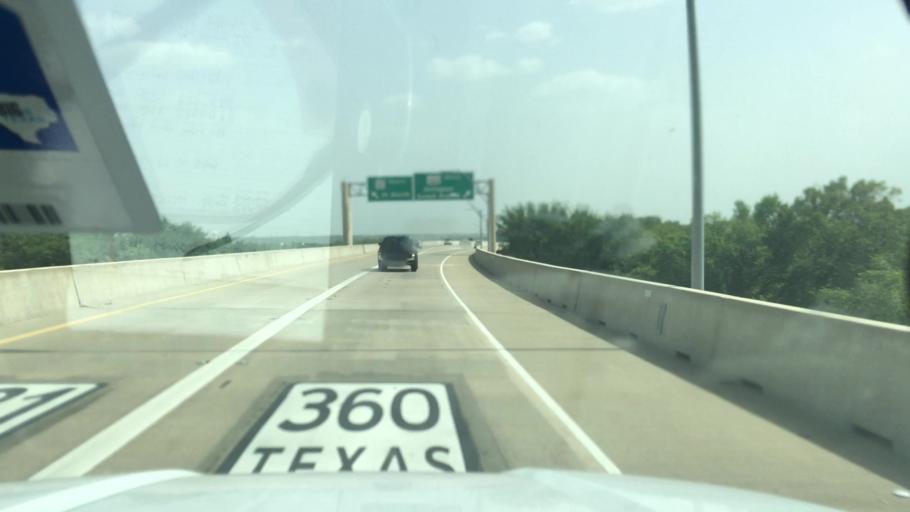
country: US
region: Texas
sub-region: Tarrant County
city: Grapevine
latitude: 32.9225
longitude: -97.0928
